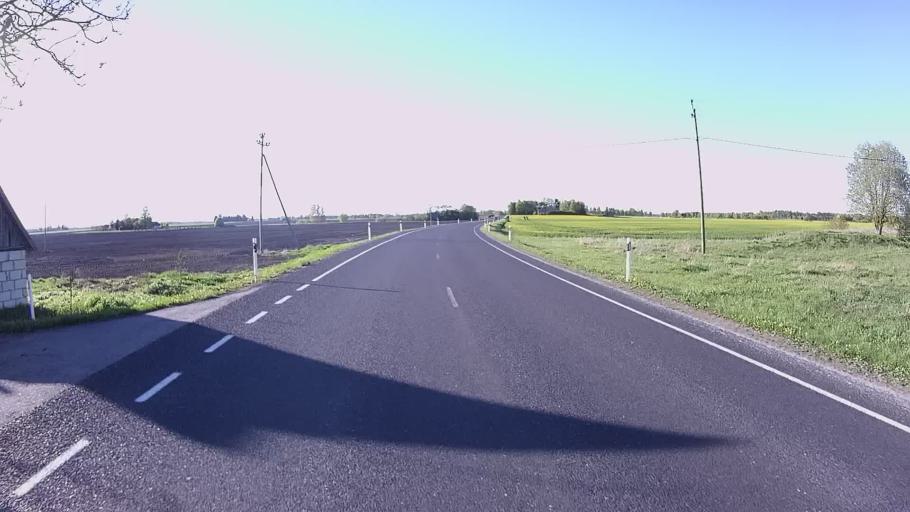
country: EE
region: Viljandimaa
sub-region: Vohma linn
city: Vohma
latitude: 58.6620
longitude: 25.6082
